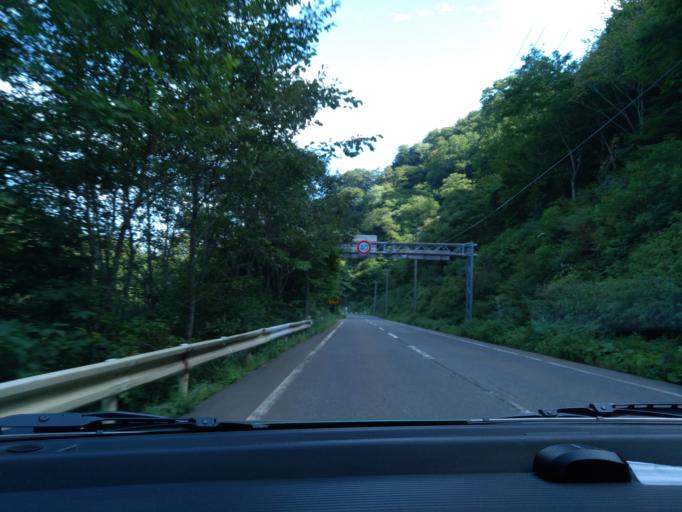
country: JP
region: Iwate
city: Shizukuishi
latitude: 39.6307
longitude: 141.0567
